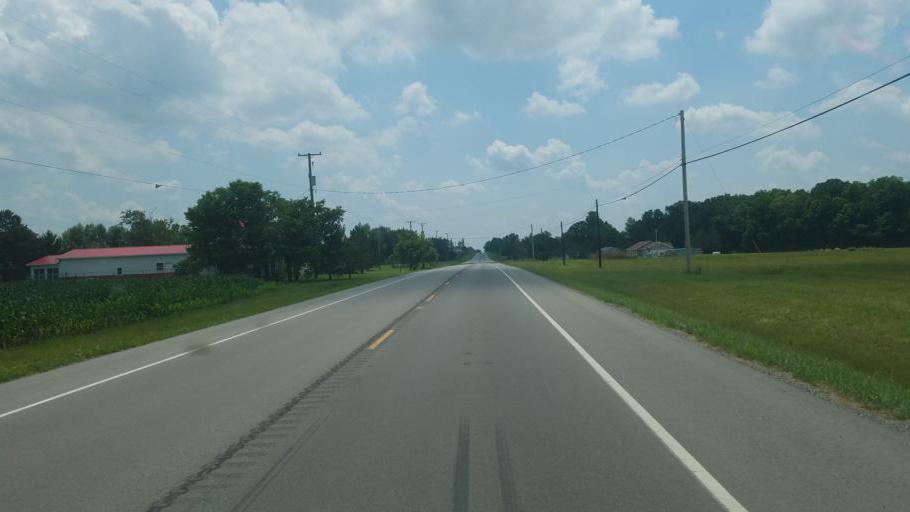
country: US
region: Ohio
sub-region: Hardin County
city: Kenton
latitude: 40.6027
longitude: -83.6342
